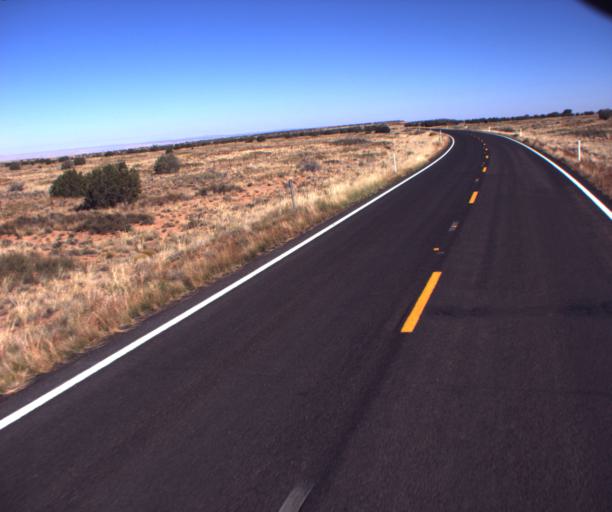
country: US
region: Arizona
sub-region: Coconino County
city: Tuba City
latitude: 35.9166
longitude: -110.8601
